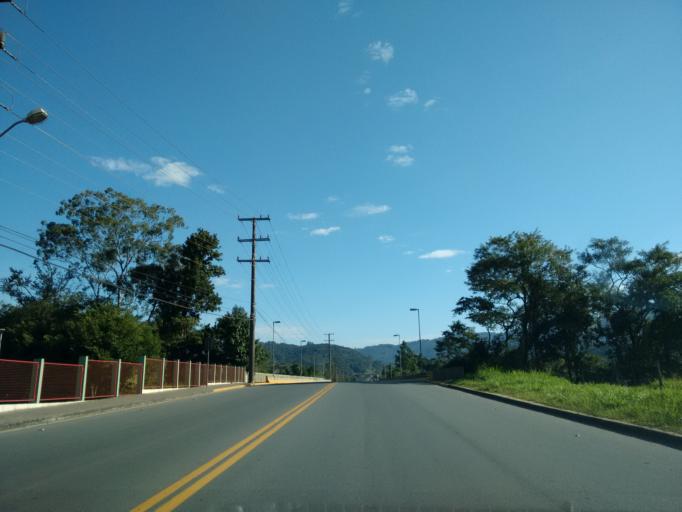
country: BR
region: Santa Catarina
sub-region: Timbo
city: Timbo
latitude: -26.8518
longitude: -49.2656
